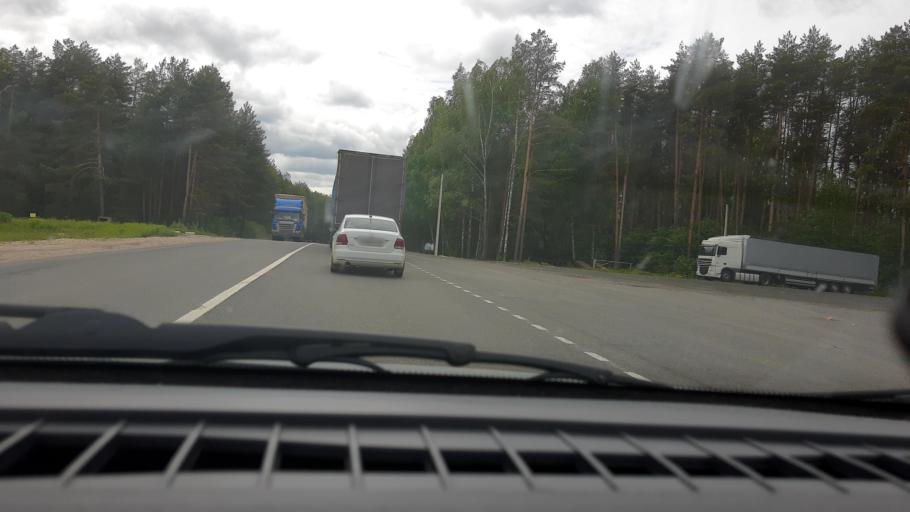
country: RU
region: Nizjnij Novgorod
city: Semenov
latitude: 56.8208
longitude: 44.5759
